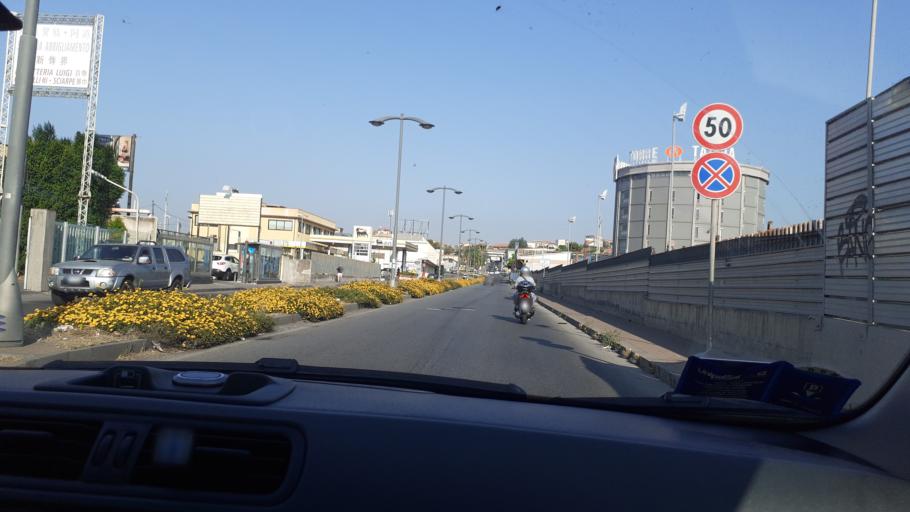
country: IT
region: Sicily
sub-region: Catania
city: Misterbianco
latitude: 37.5141
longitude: 15.0258
